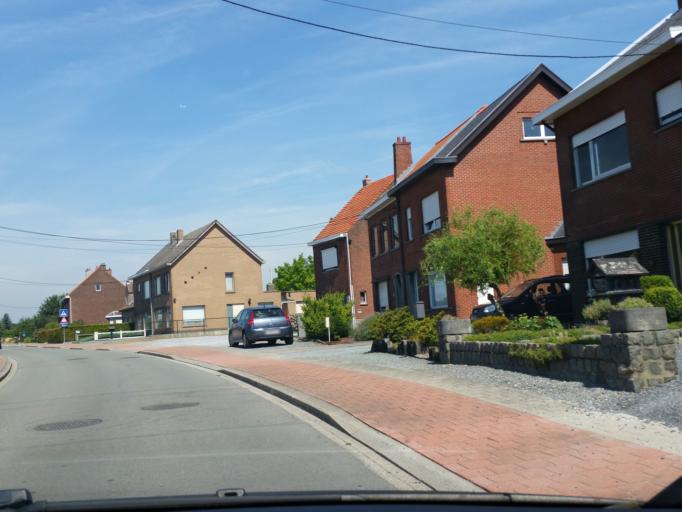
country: BE
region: Flanders
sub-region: Provincie Vlaams-Brabant
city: Zemst
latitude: 50.9697
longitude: 4.4538
